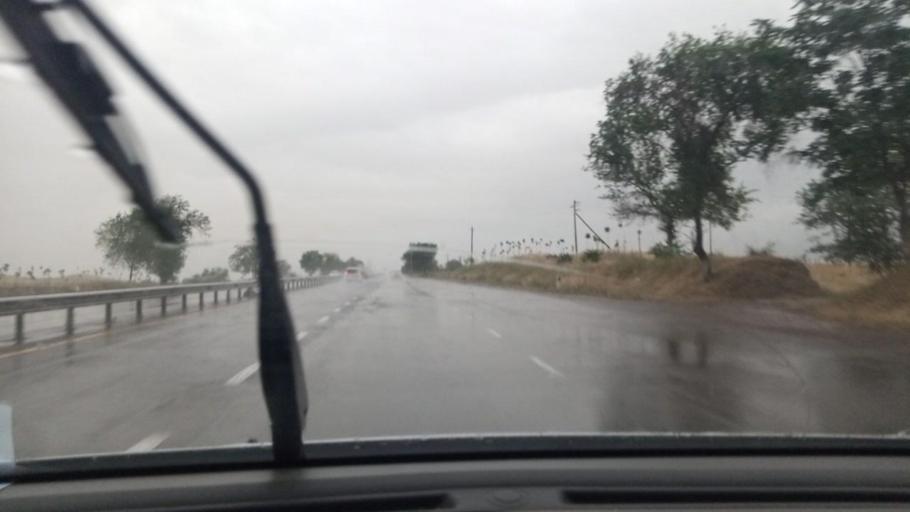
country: UZ
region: Toshkent
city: Ohangaron
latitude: 40.9873
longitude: 69.5357
